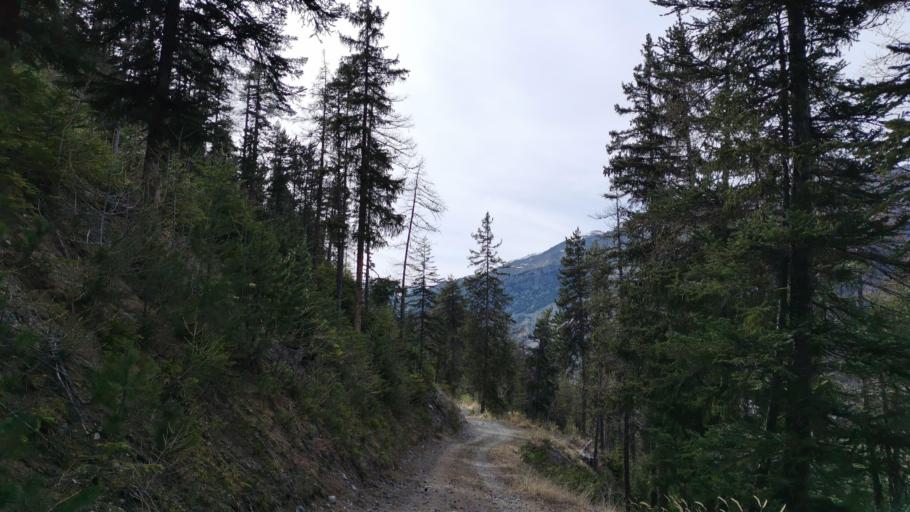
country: IT
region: Piedmont
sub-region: Provincia di Torino
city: Bardonecchia
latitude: 45.0139
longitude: 6.6415
